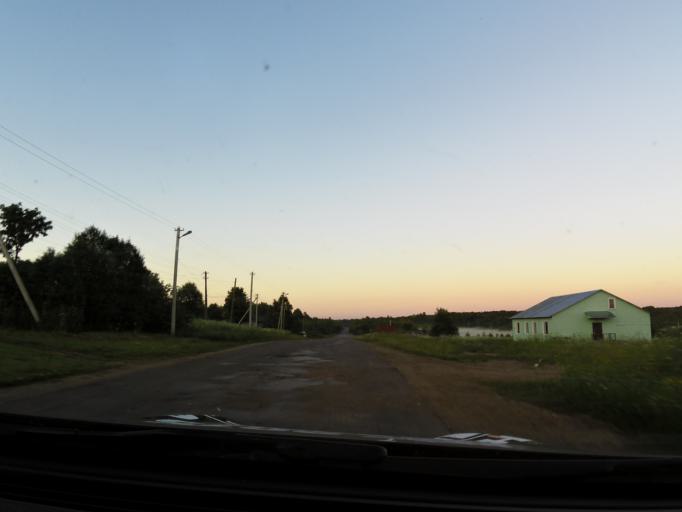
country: RU
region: Leningrad
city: Voznesen'ye
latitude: 60.8494
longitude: 35.5776
